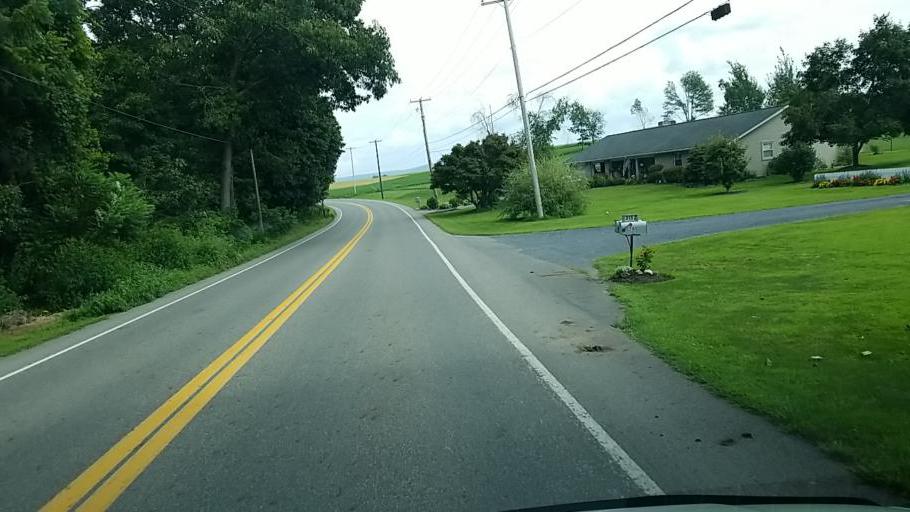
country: US
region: Pennsylvania
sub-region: Dauphin County
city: Elizabethville
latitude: 40.5842
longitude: -76.8565
